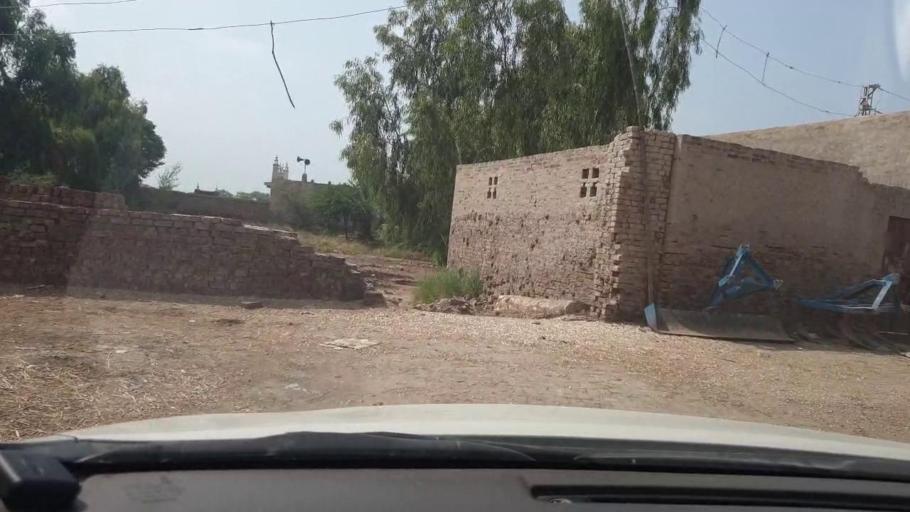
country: PK
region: Sindh
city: Shikarpur
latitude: 27.9918
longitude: 68.5842
